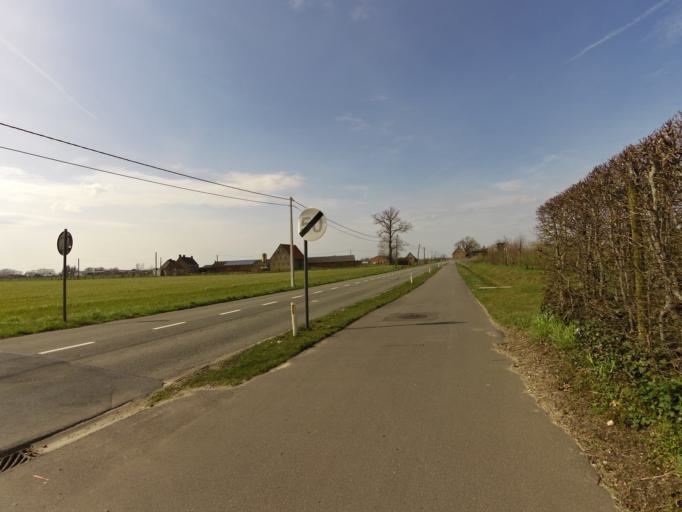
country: BE
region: Flanders
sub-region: Provincie West-Vlaanderen
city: Koekelare
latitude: 51.0994
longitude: 2.9785
